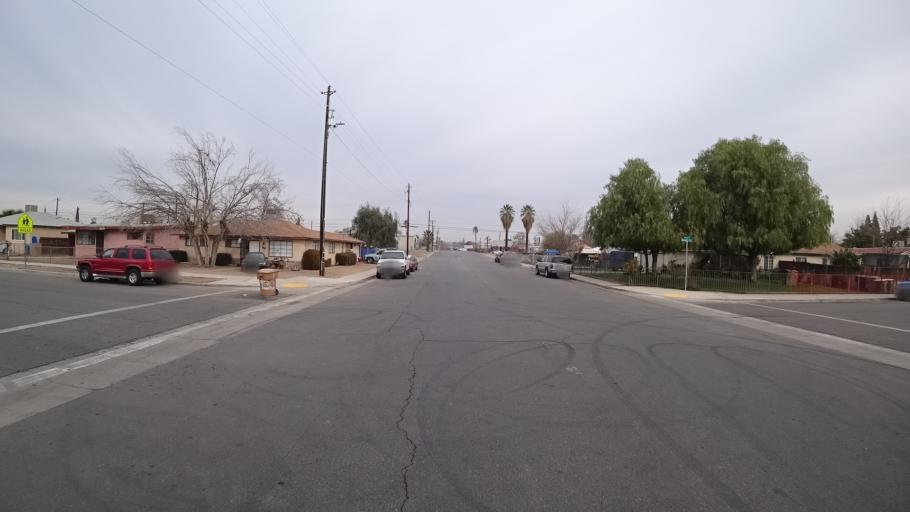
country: US
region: California
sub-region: Kern County
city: Bakersfield
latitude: 35.3715
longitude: -118.9898
